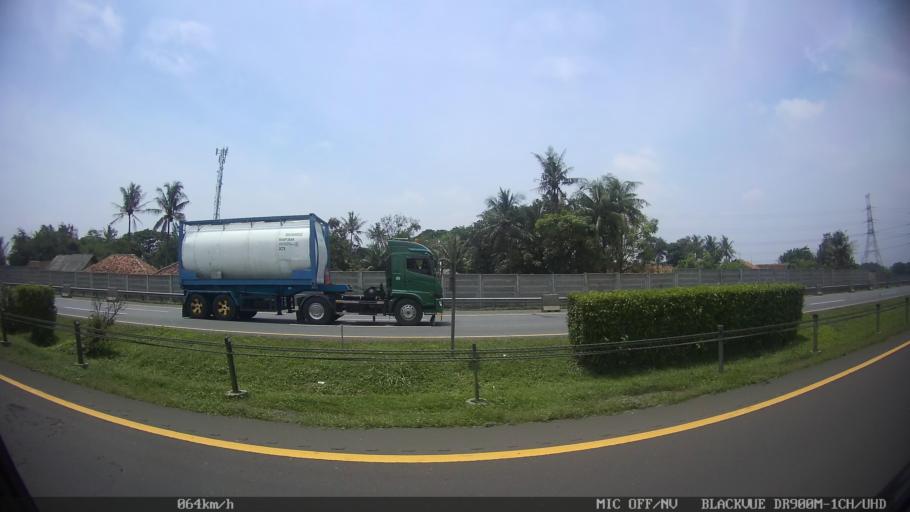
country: ID
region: West Java
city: Kresek
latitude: -6.1918
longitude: 106.4147
